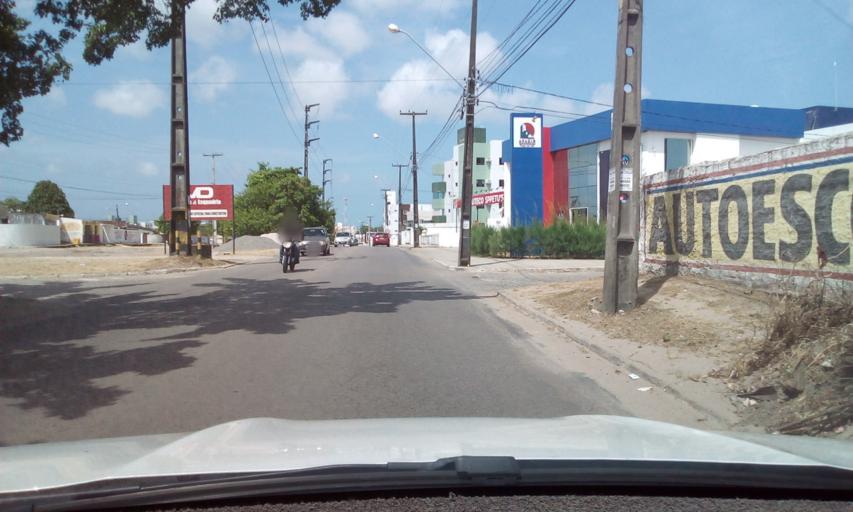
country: BR
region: Paraiba
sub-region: Joao Pessoa
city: Joao Pessoa
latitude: -7.1801
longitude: -34.8651
